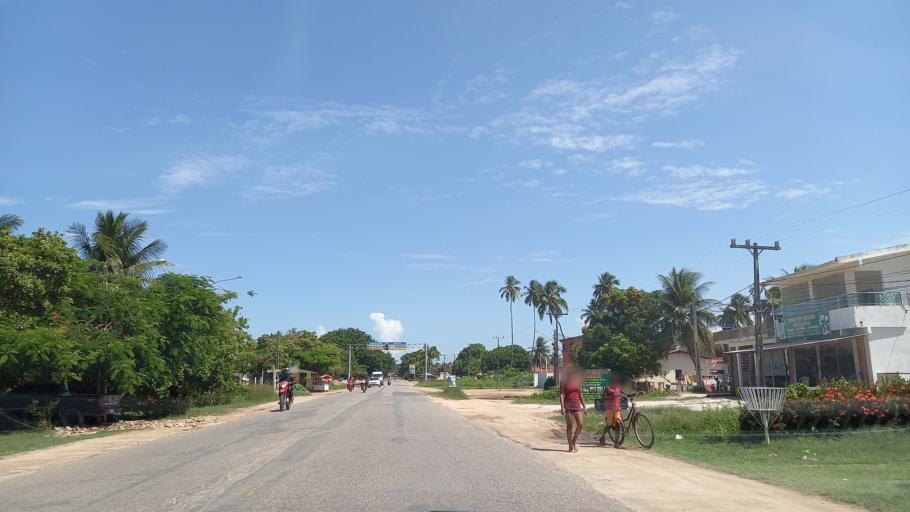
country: BR
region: Pernambuco
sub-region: Sao Jose Da Coroa Grande
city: Sao Jose da Coroa Grande
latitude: -8.9080
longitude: -35.1526
